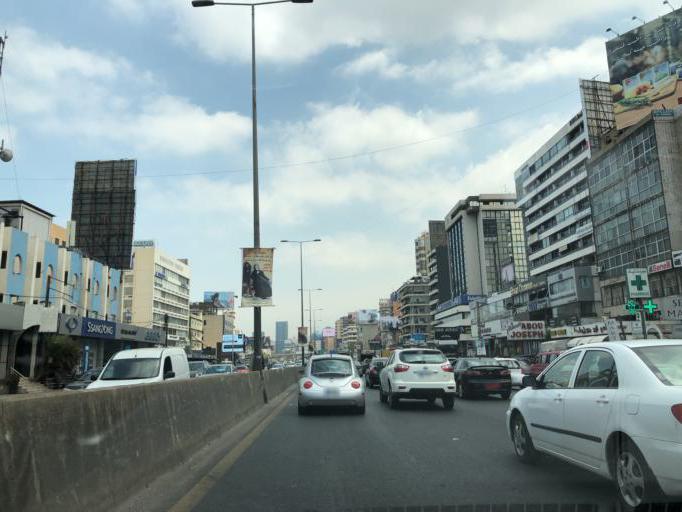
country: LB
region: Mont-Liban
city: Jdaidet el Matn
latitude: 33.9057
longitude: 35.5753
